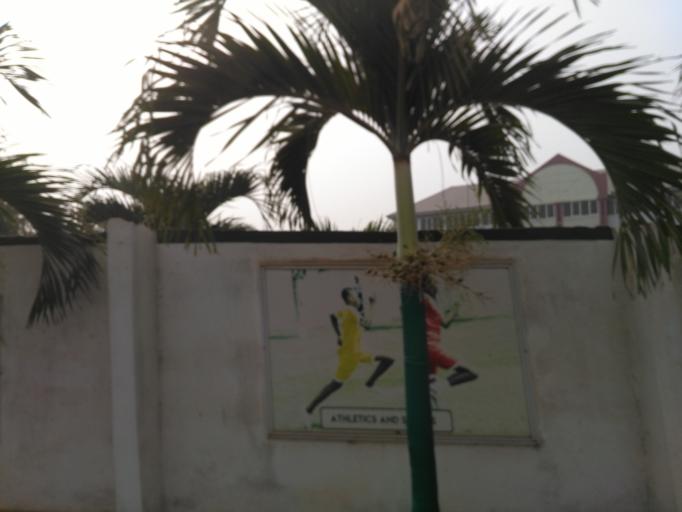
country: GH
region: Ashanti
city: Kumasi
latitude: 6.6517
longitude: -1.6246
